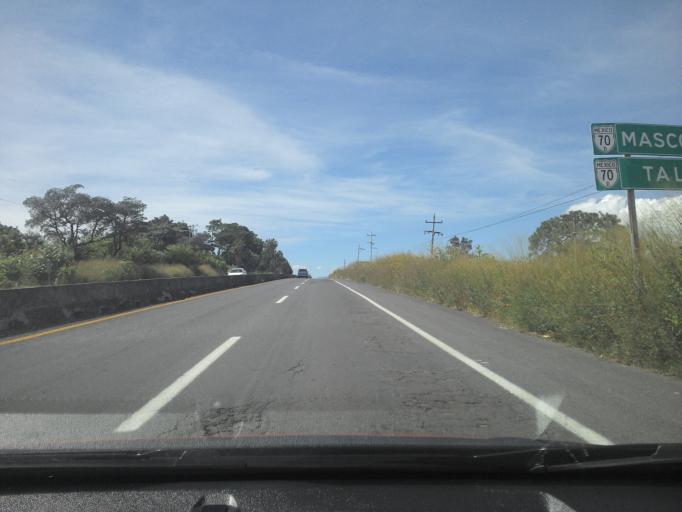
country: MX
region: Jalisco
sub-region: Tala
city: Los Ruisenores
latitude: 20.7174
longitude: -103.6382
